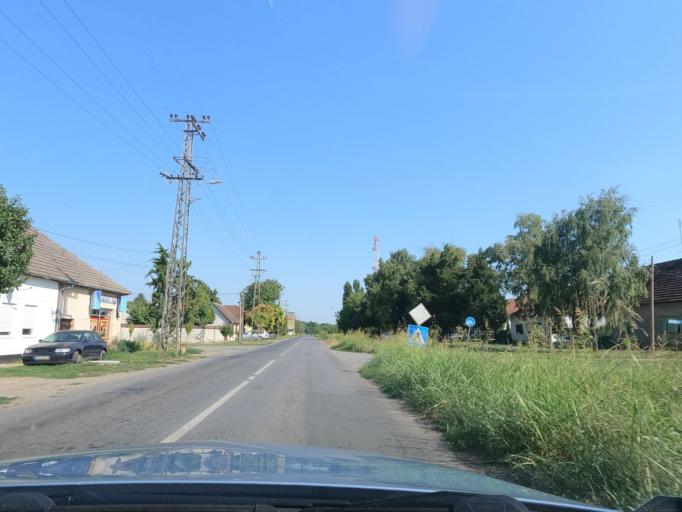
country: RS
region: Autonomna Pokrajina Vojvodina
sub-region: Juznobacki Okrug
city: Becej
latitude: 45.6256
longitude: 20.0280
